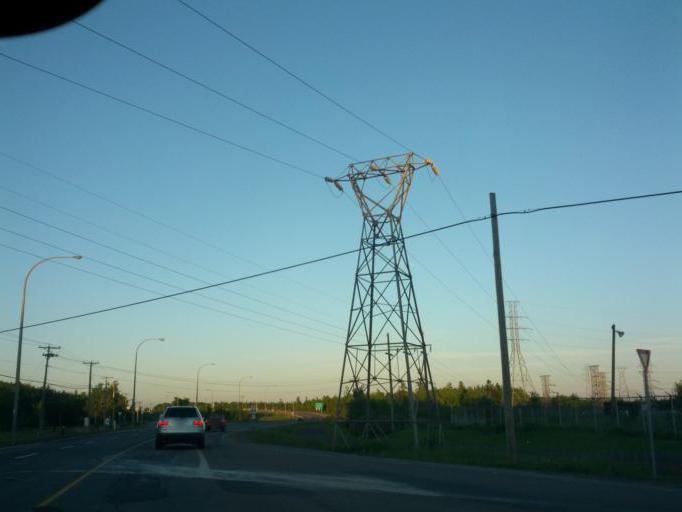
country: CA
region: New Brunswick
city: Moncton
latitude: 46.0959
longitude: -64.8460
